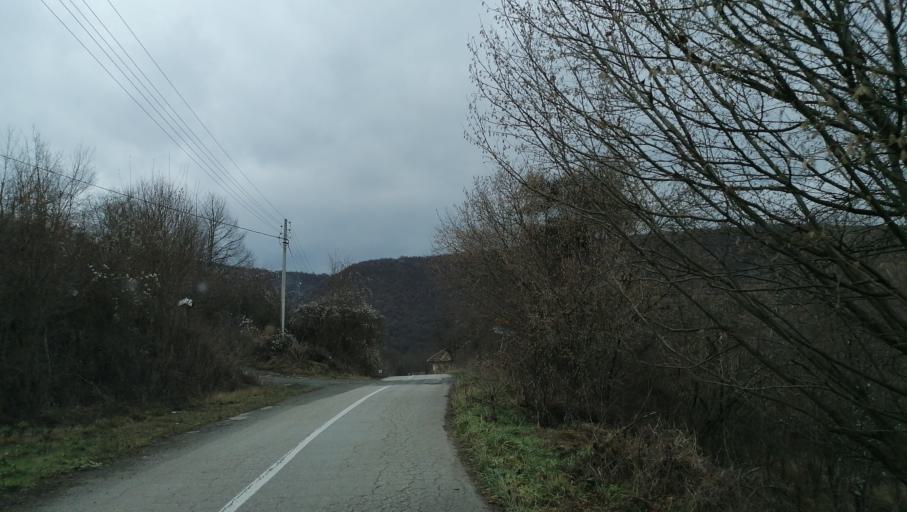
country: RS
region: Central Serbia
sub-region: Pirotski Okrug
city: Dimitrovgrad
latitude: 42.9290
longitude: 22.7717
